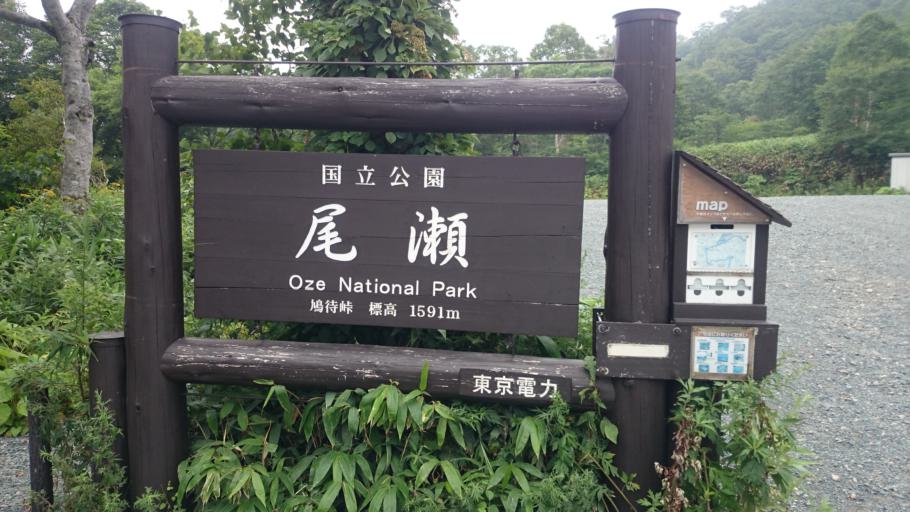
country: JP
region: Gunma
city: Numata
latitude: 36.8903
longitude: 139.2004
